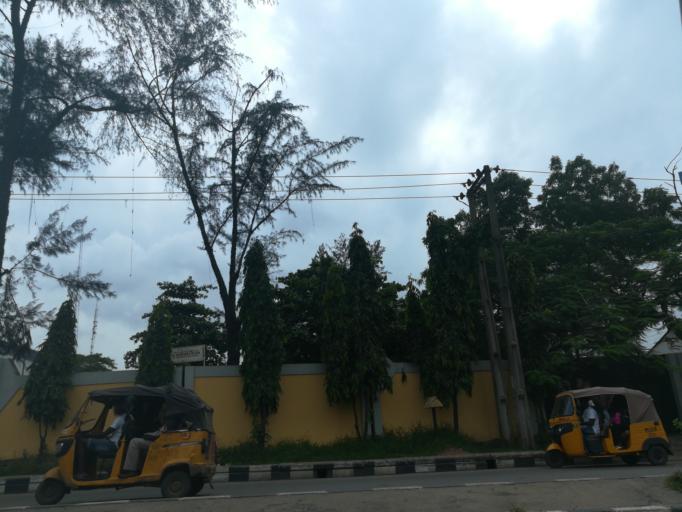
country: NG
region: Lagos
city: Ikeja
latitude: 6.6048
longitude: 3.3614
